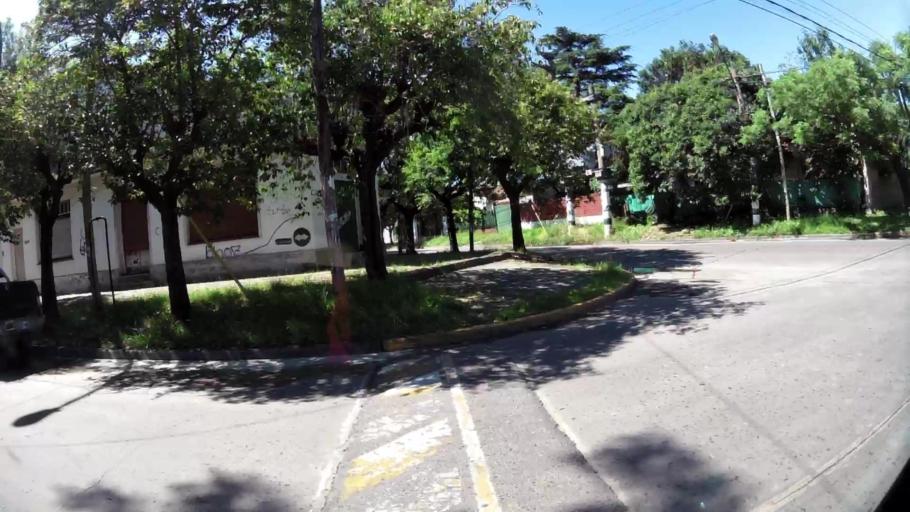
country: AR
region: Buenos Aires
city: Ituzaingo
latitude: -34.6649
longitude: -58.6663
